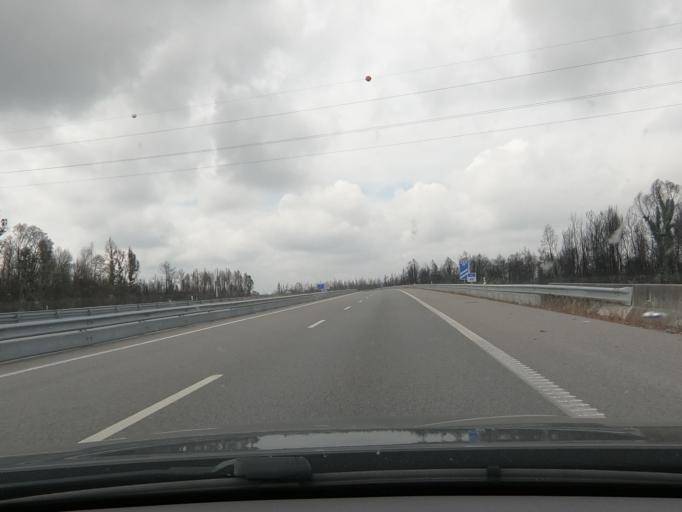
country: PT
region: Coimbra
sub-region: Mira
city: Mira
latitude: 40.4216
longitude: -8.7089
